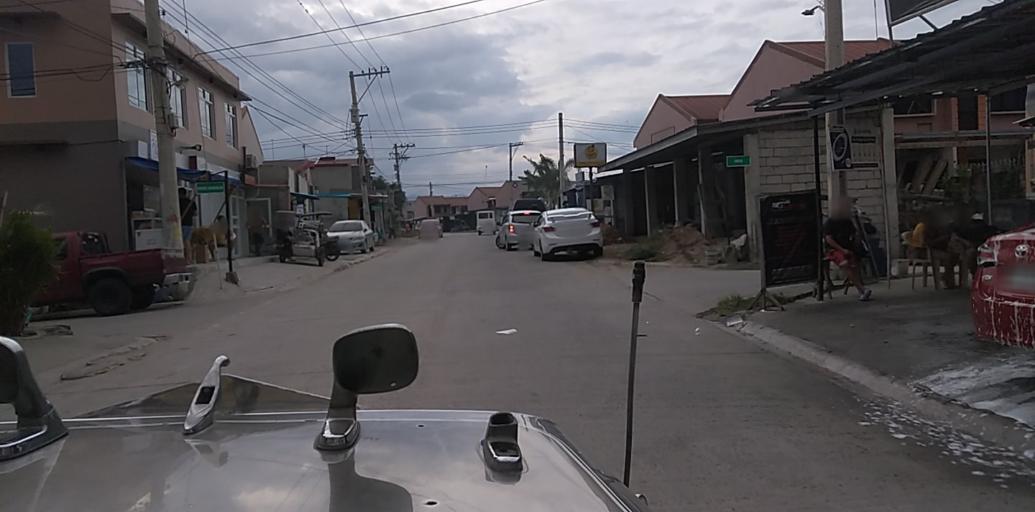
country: PH
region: Central Luzon
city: Santol
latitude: 15.1665
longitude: 120.5341
